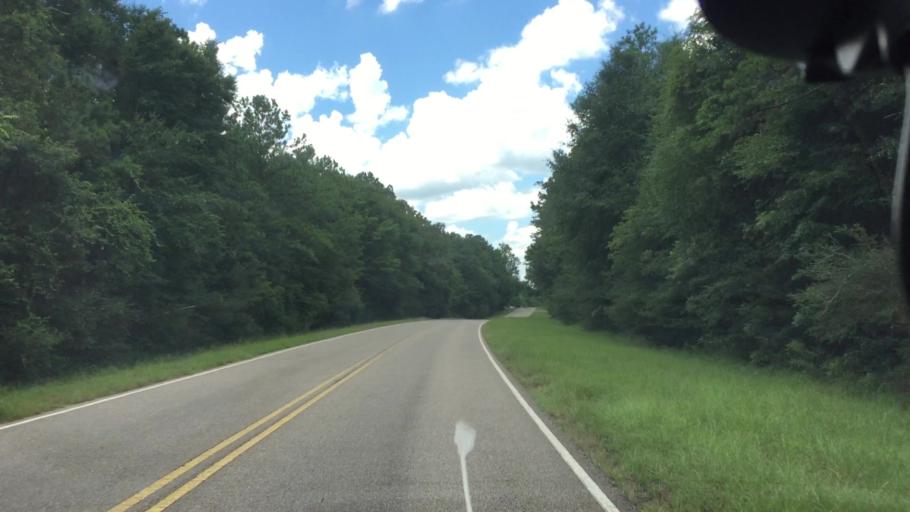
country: US
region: Alabama
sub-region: Coffee County
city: New Brockton
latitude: 31.4095
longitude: -85.8507
